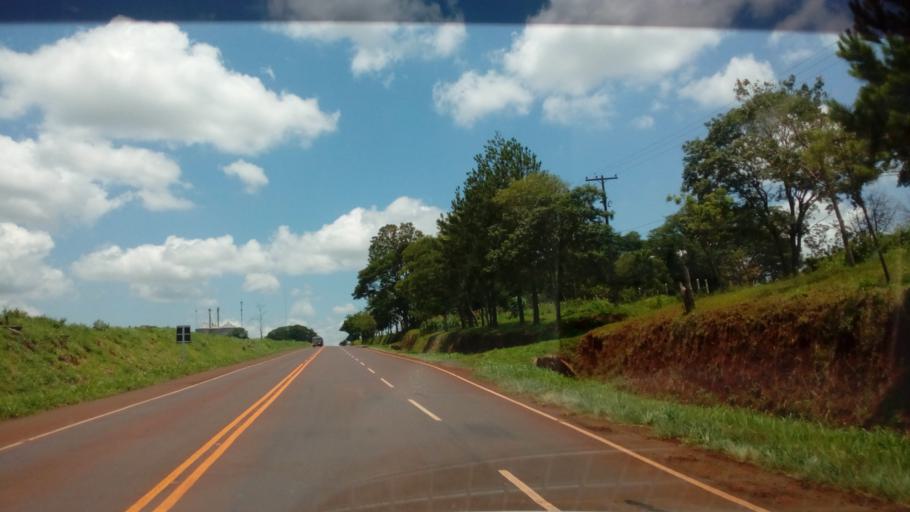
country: PY
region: Itapua
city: Arquitecto Tomas Romero Pereira
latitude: -26.3515
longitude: -55.2331
